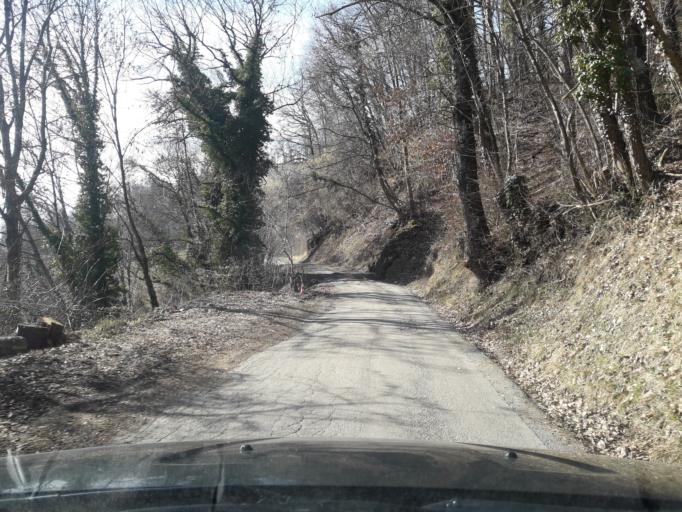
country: FR
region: Rhone-Alpes
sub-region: Departement de l'Isere
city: Corenc
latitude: 45.2257
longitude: 5.7495
